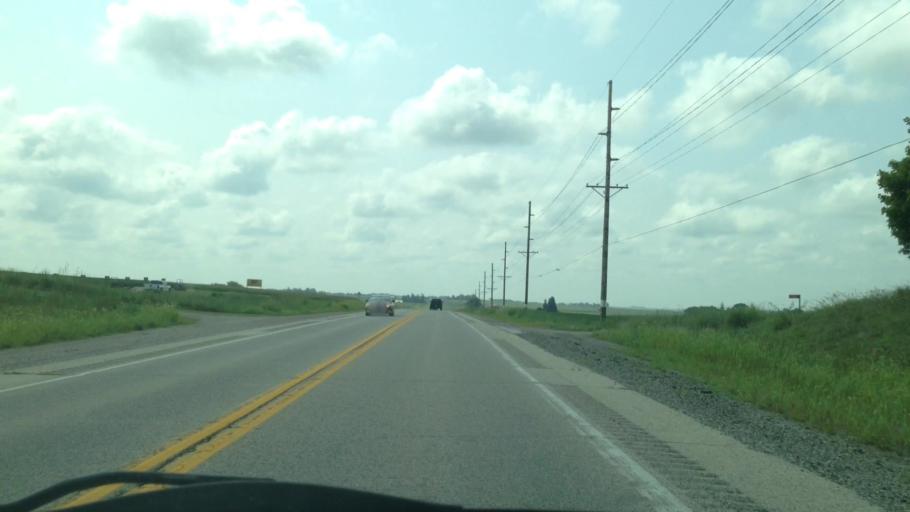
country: US
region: Iowa
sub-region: Benton County
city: Walford
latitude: 41.8715
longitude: -91.8703
